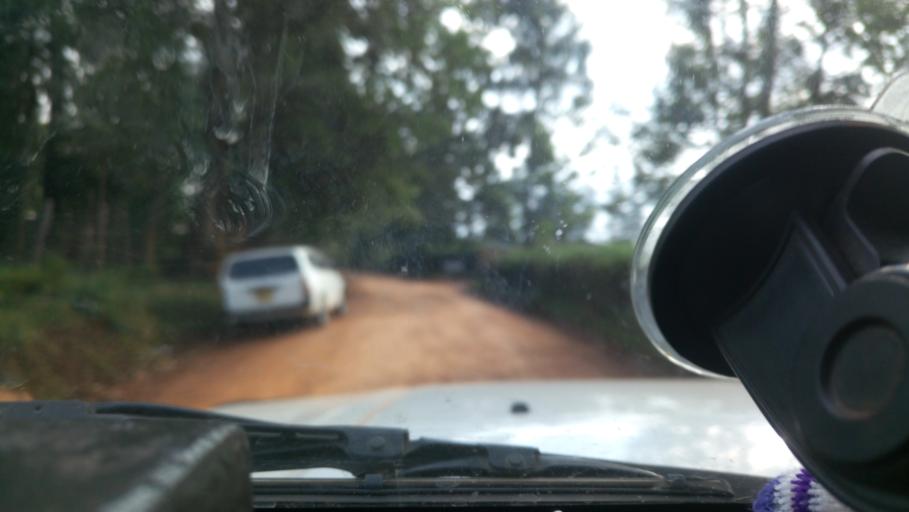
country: KE
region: Kericho
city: Litein
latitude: -0.5646
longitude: 35.1911
